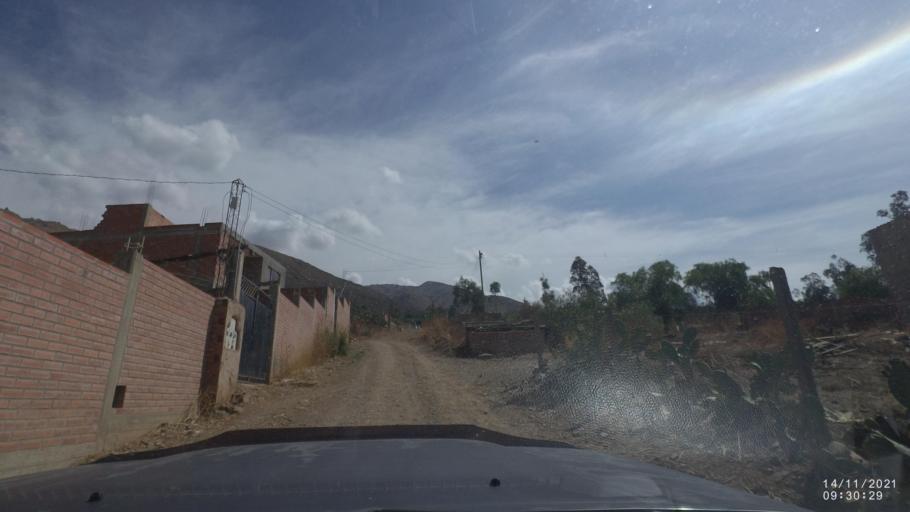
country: BO
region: Cochabamba
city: Cochabamba
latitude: -17.3702
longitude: -66.0905
